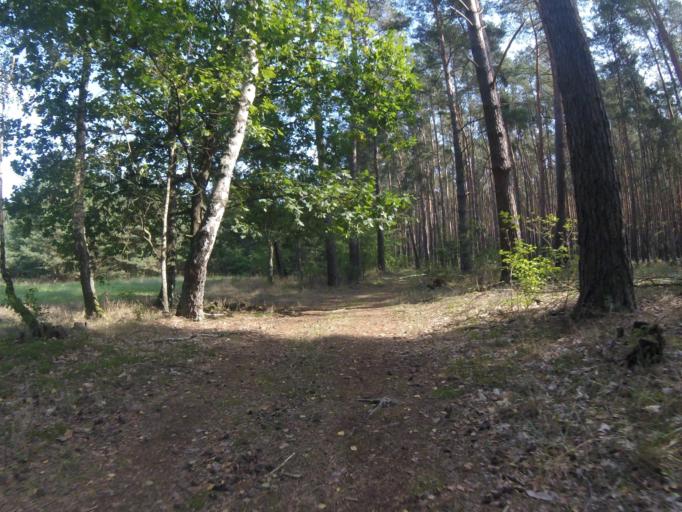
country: DE
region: Brandenburg
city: Bestensee
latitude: 52.2805
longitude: 13.7097
